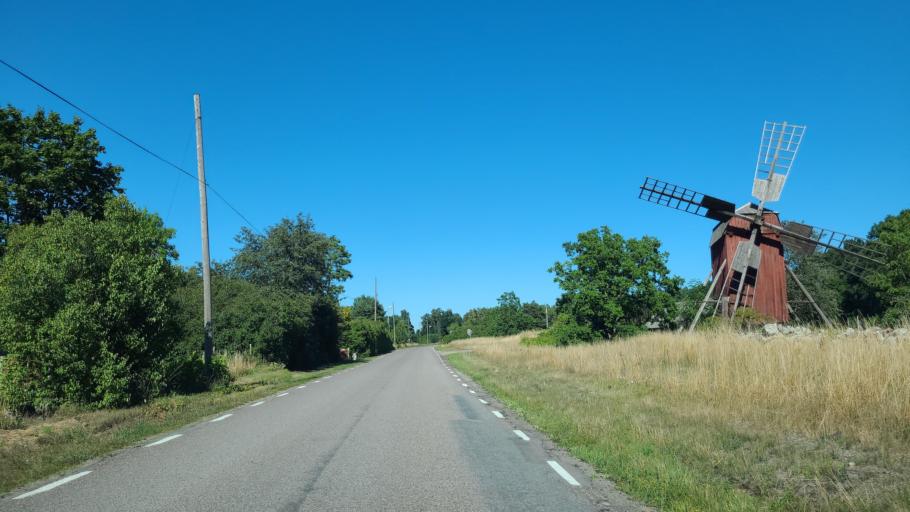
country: SE
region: Kalmar
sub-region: Borgholms Kommun
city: Borgholm
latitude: 56.8347
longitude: 16.7765
